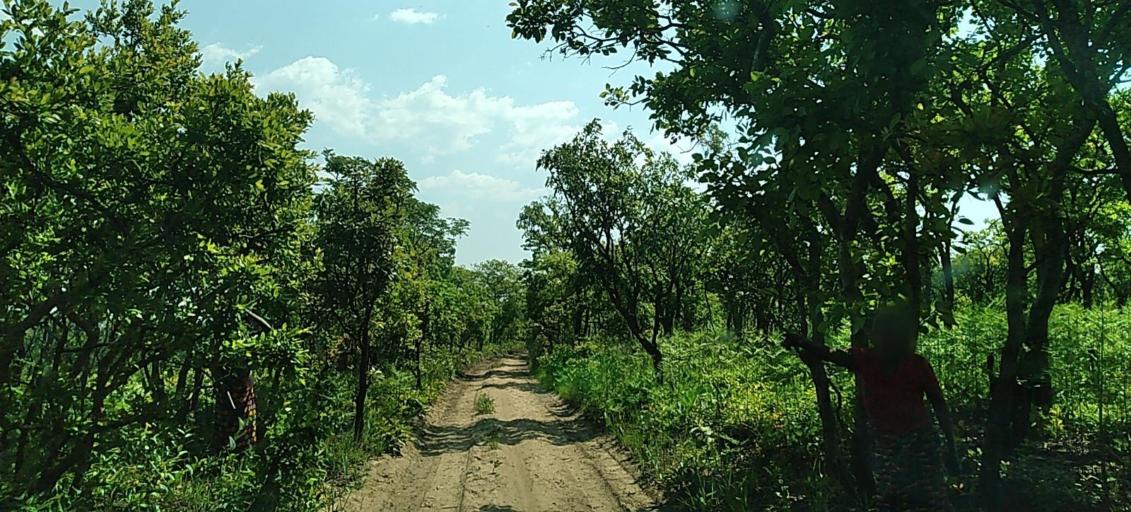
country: CD
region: Katanga
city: Kolwezi
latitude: -11.2642
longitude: 25.0024
